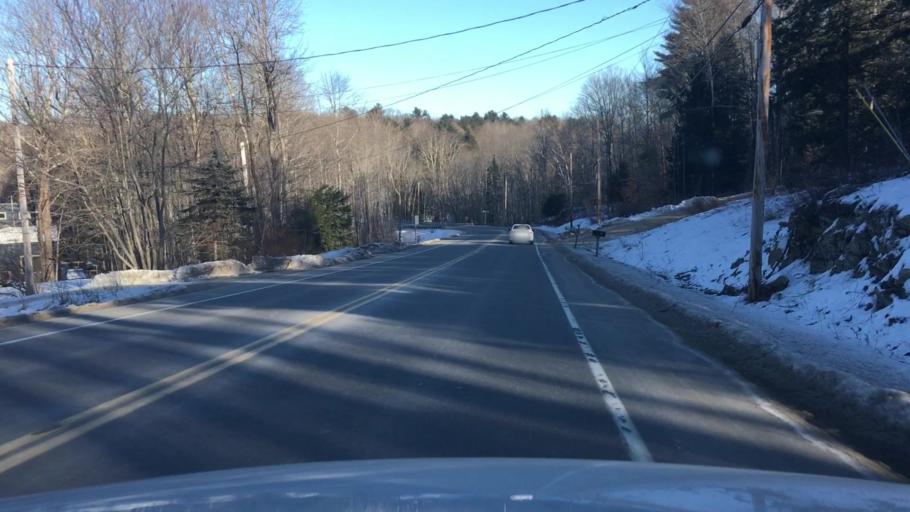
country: US
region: Maine
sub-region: Cumberland County
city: Freeport
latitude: 43.8971
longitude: -70.1141
